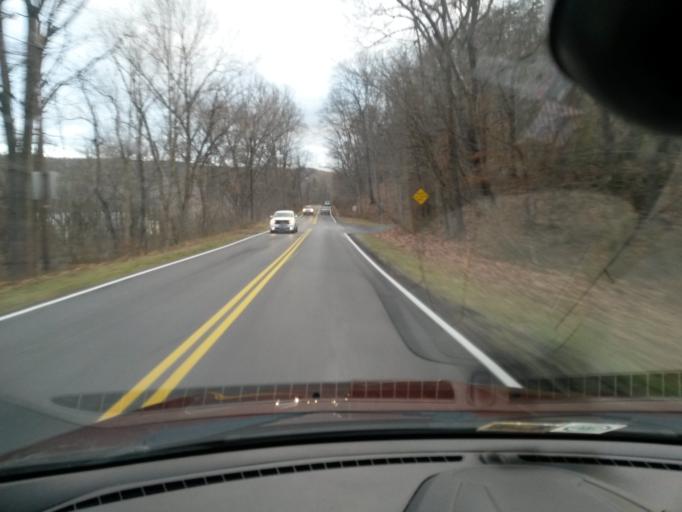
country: US
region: Virginia
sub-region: City of Covington
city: Fairlawn
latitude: 37.7693
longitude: -79.9928
